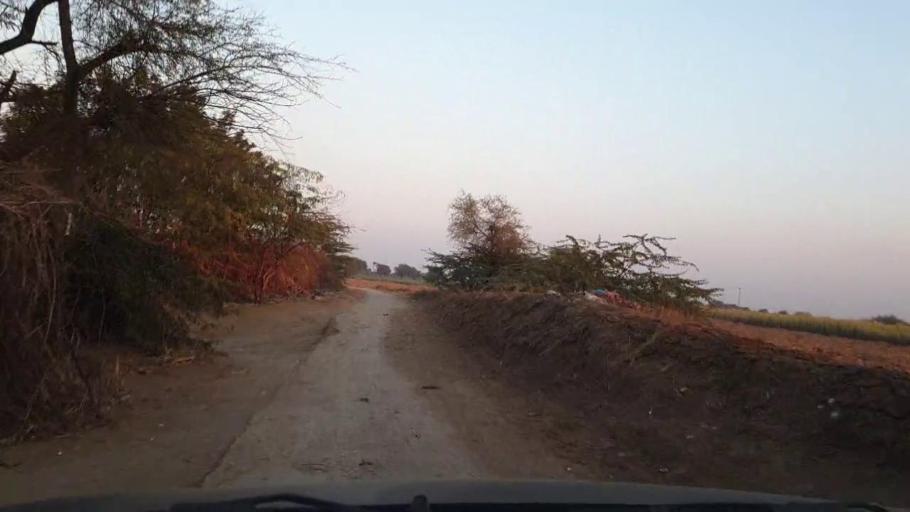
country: PK
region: Sindh
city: Jhol
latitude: 25.9289
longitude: 68.9768
